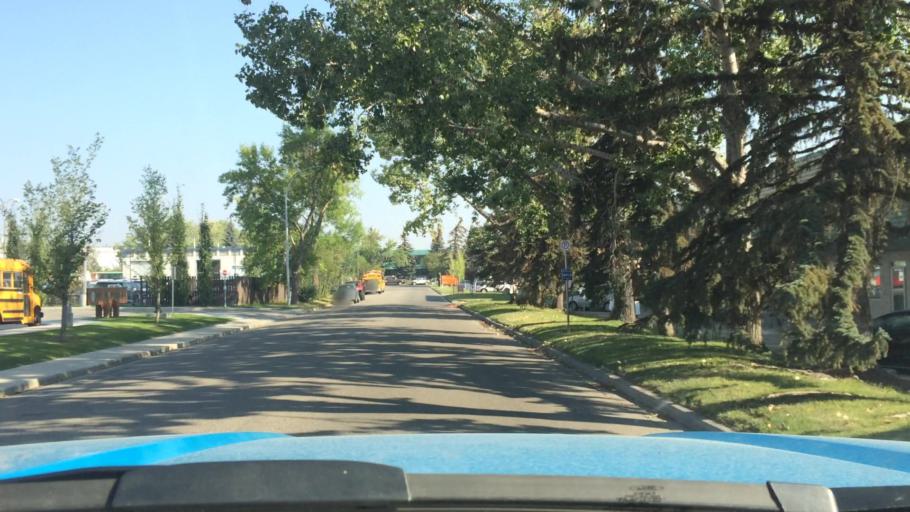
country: CA
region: Alberta
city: Calgary
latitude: 50.9870
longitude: -114.0498
